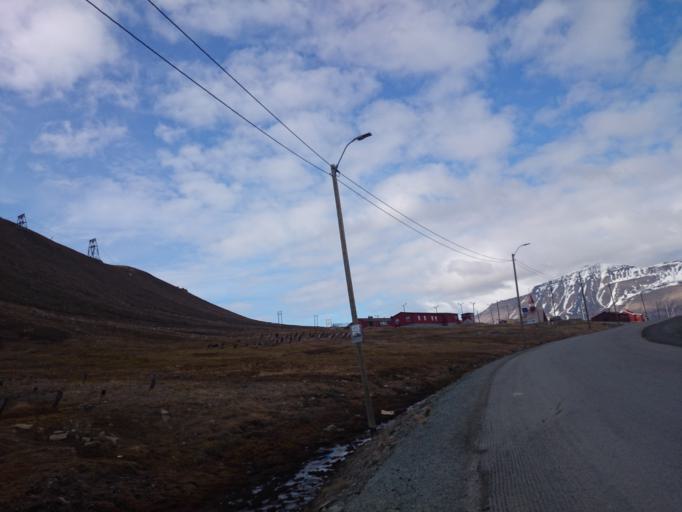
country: SJ
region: Svalbard
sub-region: Spitsbergen
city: Longyearbyen
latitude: 78.2173
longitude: 15.6190
